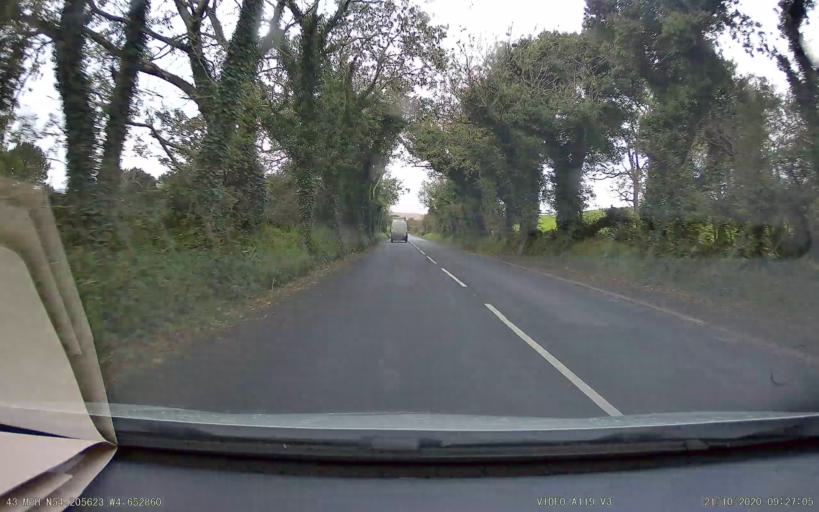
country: IM
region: Castletown
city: Castletown
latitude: 54.2056
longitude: -4.6529
